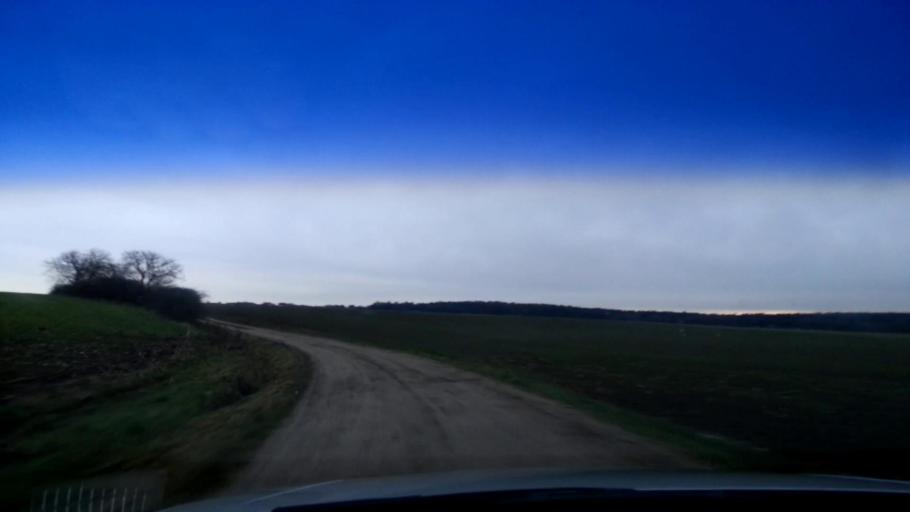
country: DE
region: Bavaria
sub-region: Upper Franconia
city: Litzendorf
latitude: 49.9187
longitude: 10.9886
